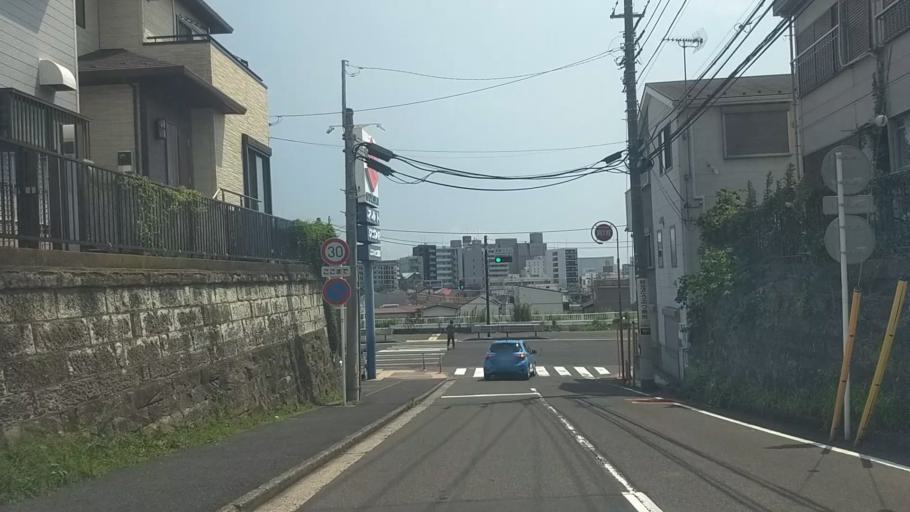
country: JP
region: Kanagawa
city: Yokohama
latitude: 35.4849
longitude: 139.6378
